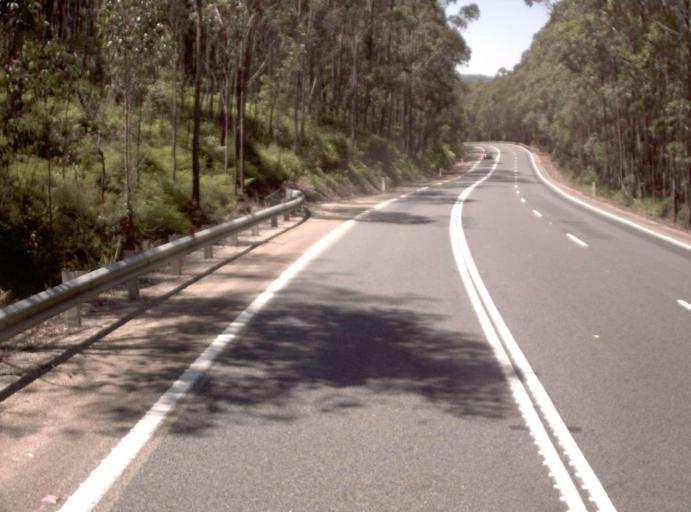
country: AU
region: New South Wales
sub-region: Bombala
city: Bombala
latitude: -37.6119
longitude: 148.8897
